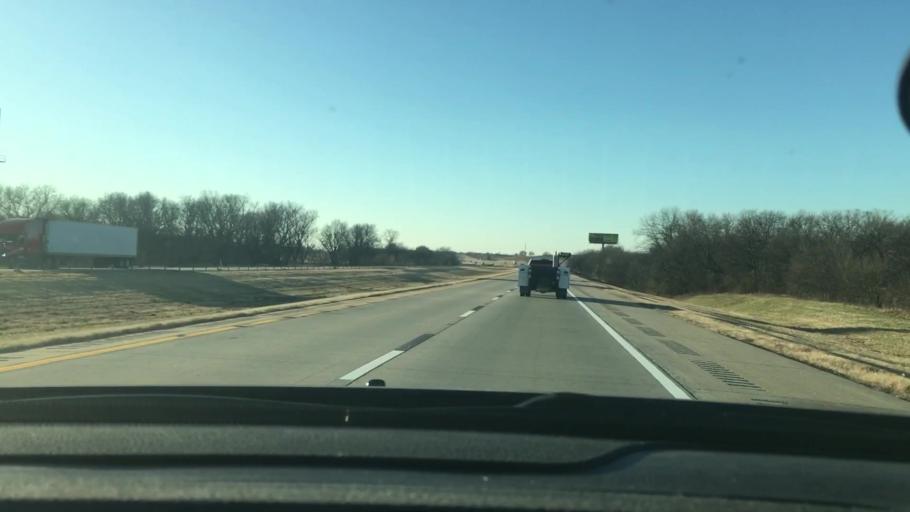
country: US
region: Oklahoma
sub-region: Carter County
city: Ardmore
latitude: 34.2685
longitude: -97.1635
